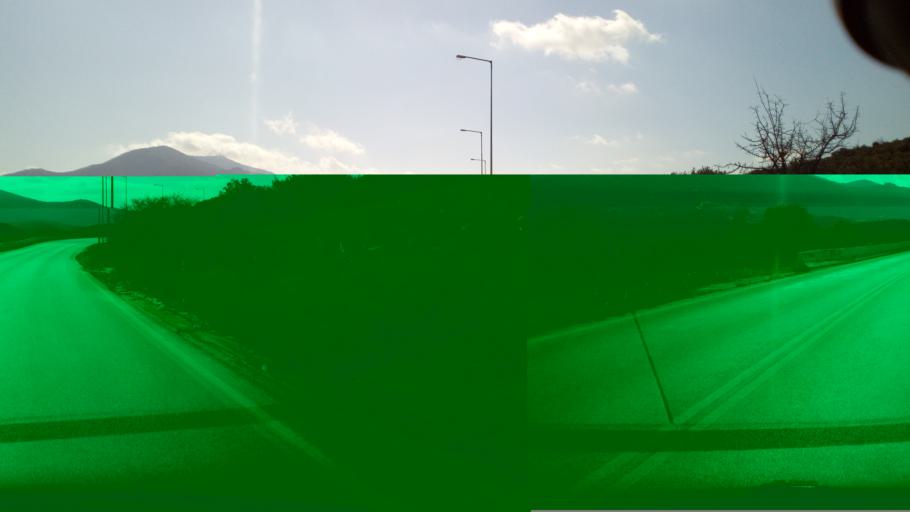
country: GR
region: Central Macedonia
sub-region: Nomos Thessalonikis
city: Chortiatis
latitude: 40.6223
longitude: 23.0644
